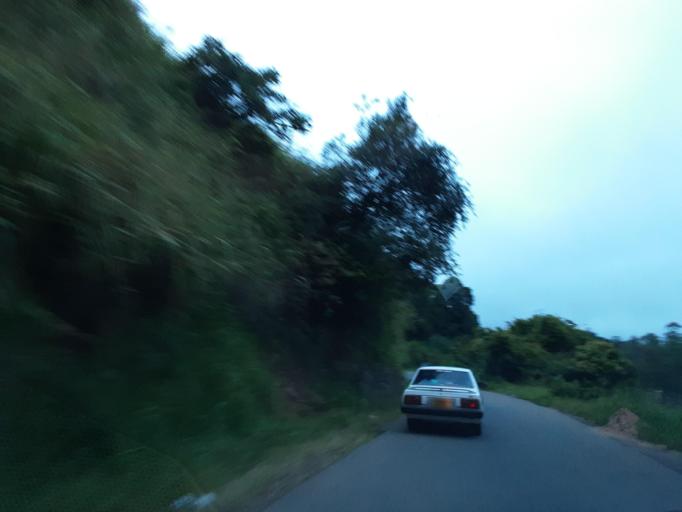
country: LK
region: Uva
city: Haputale
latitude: 6.9073
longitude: 80.9234
